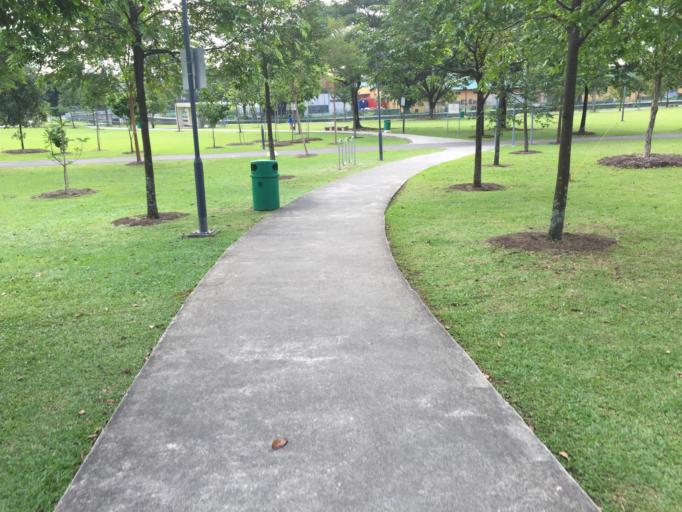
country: MY
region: Johor
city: Johor Bahru
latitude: 1.3388
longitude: 103.7077
